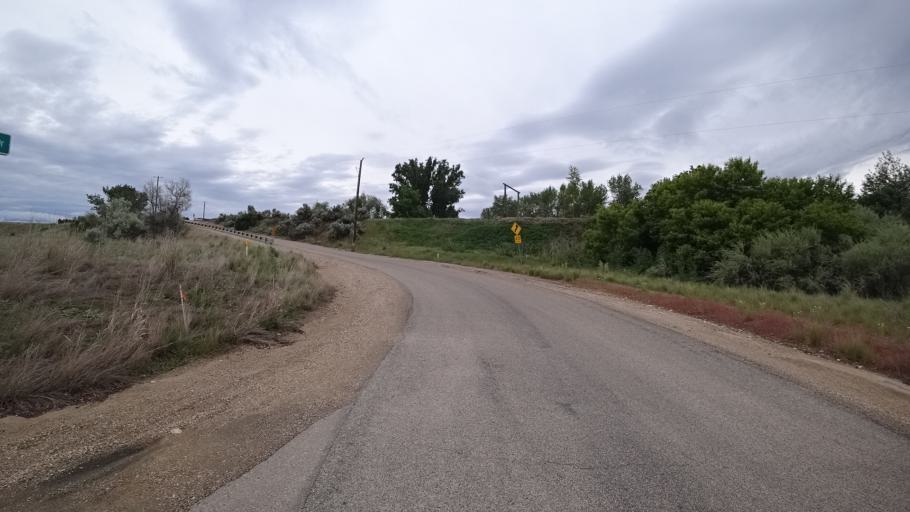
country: US
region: Idaho
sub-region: Ada County
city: Star
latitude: 43.6696
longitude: -116.4736
